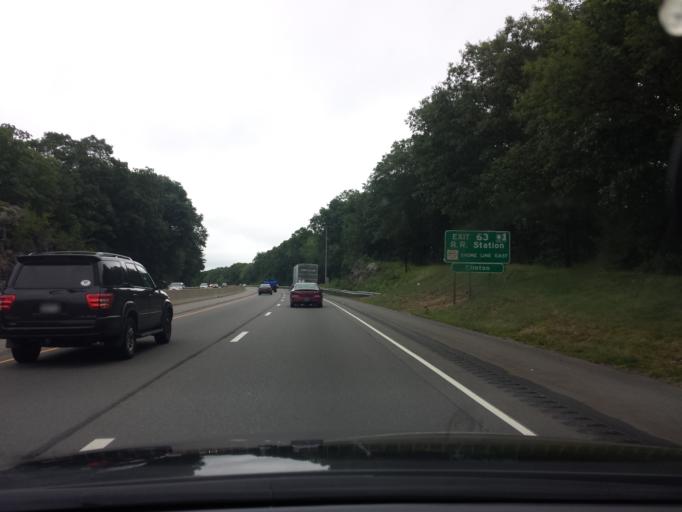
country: US
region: Connecticut
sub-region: Middlesex County
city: Clinton
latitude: 41.2887
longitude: -72.5600
